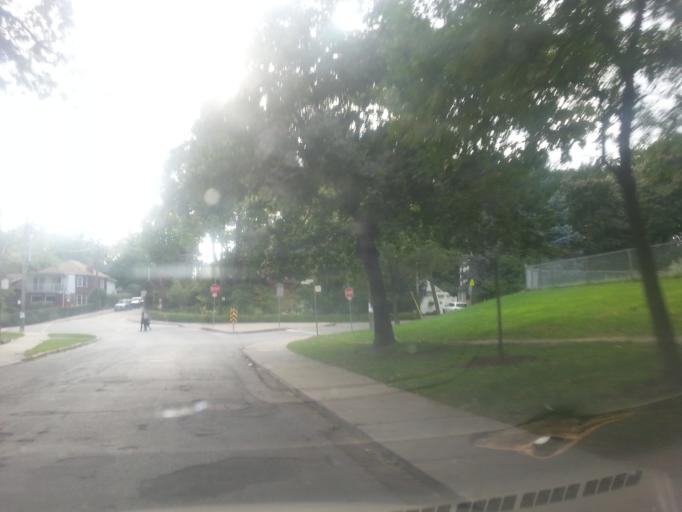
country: CA
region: Ontario
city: Toronto
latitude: 43.6587
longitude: -79.4706
